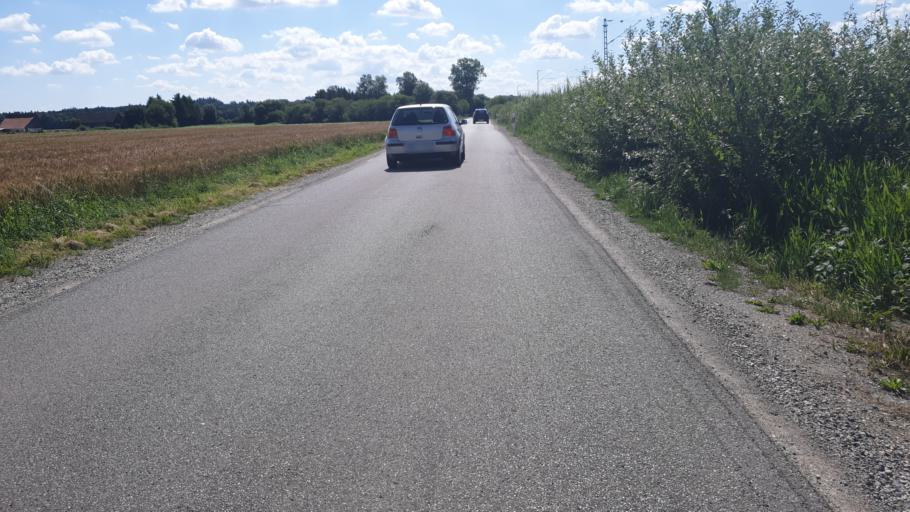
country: DE
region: Bavaria
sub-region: Upper Bavaria
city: Puchheim
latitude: 48.1674
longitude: 11.3701
